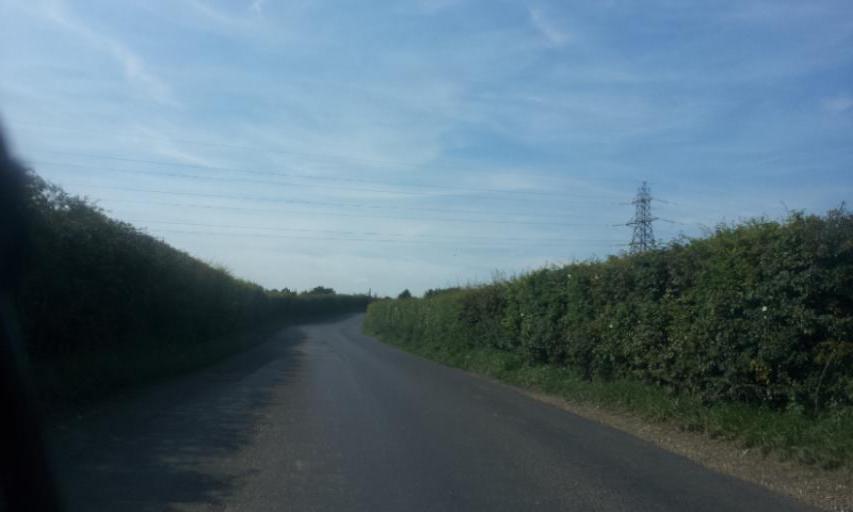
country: GB
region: England
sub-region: Kent
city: Newington
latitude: 51.3260
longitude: 0.6898
